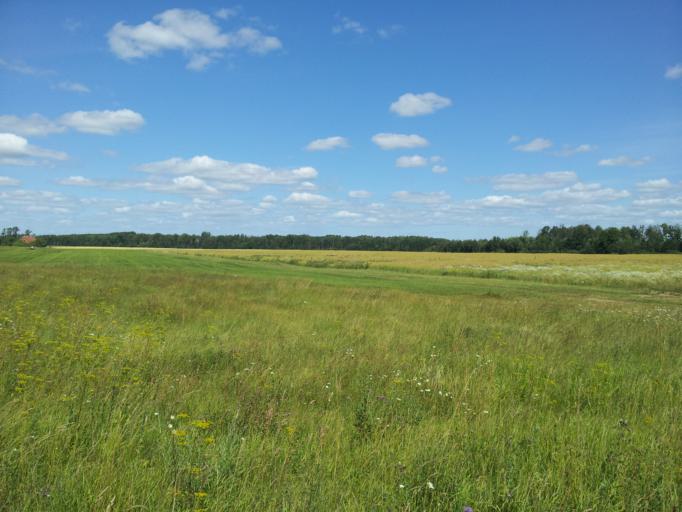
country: LV
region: Jaunpils
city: Jaunpils
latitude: 56.7889
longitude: 23.1530
